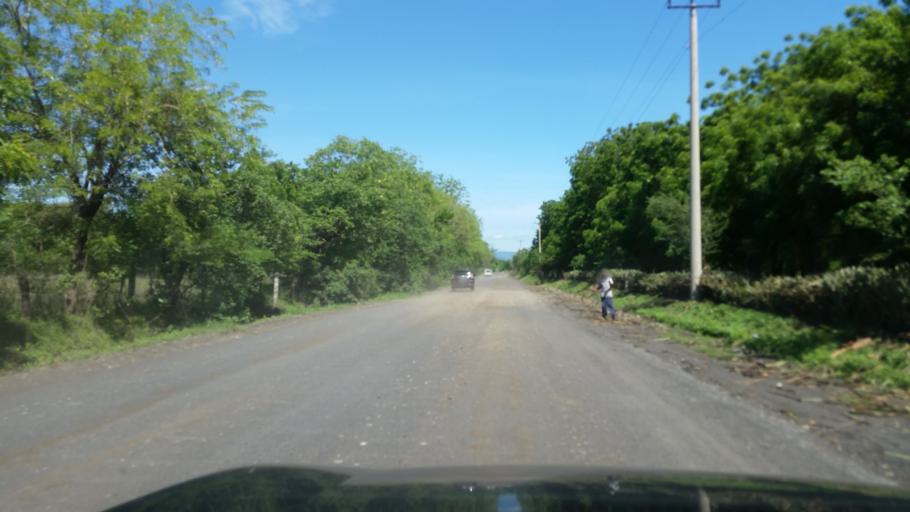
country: NI
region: Chinandega
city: Puerto Morazan
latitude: 12.7689
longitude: -87.0713
